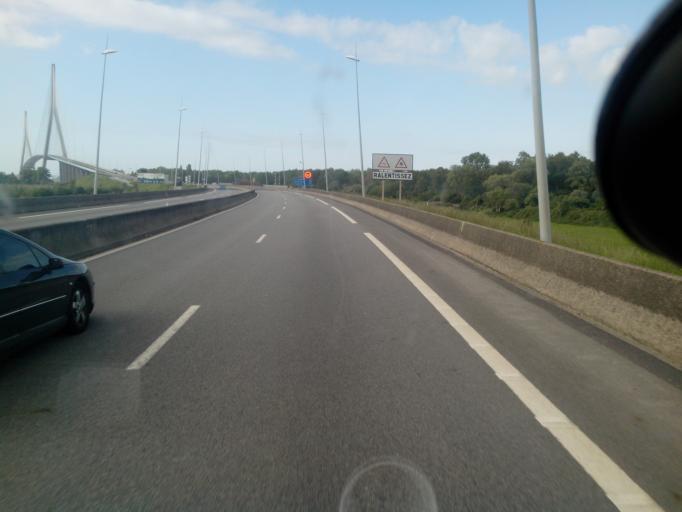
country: FR
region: Lower Normandy
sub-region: Departement du Calvados
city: La Riviere-Saint-Sauveur
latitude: 49.4175
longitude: 0.2745
